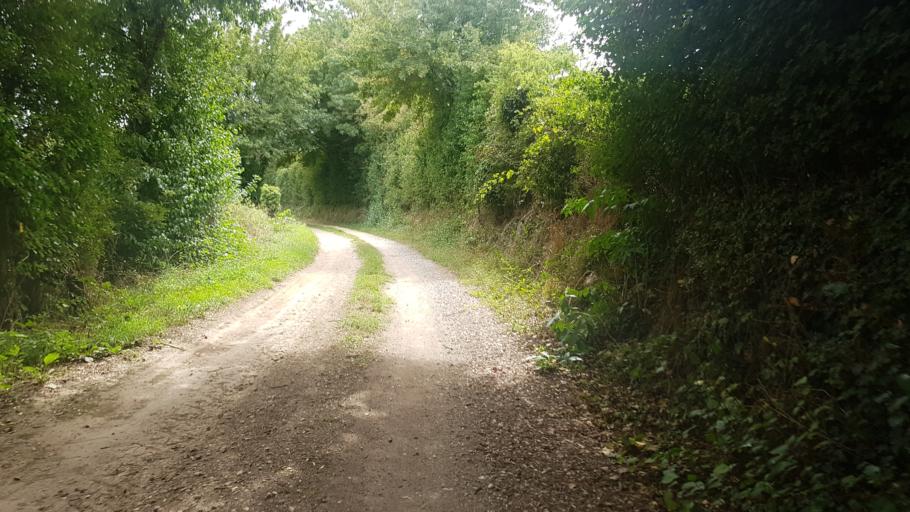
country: FR
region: Poitou-Charentes
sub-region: Departement des Deux-Sevres
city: Vouille
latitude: 46.3129
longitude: -0.3424
